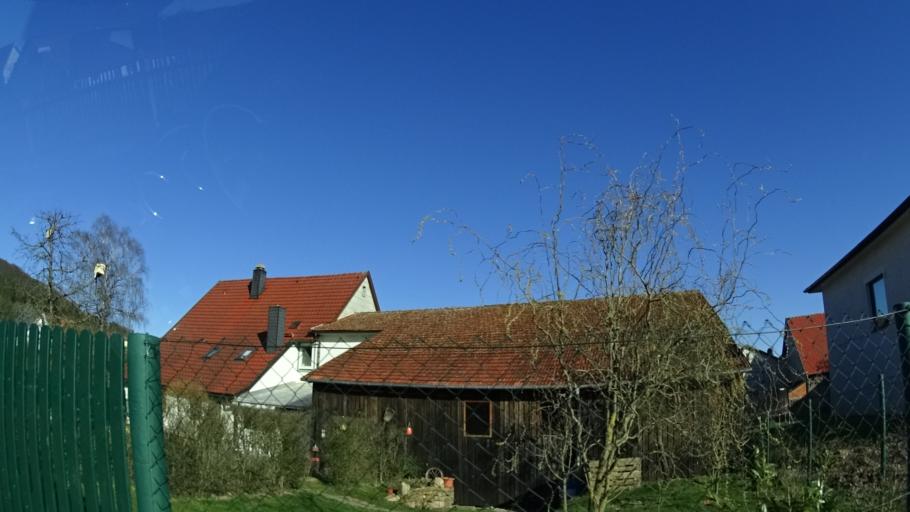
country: DE
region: Bavaria
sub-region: Regierungsbezirk Unterfranken
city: Willmars
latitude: 50.5287
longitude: 10.2874
